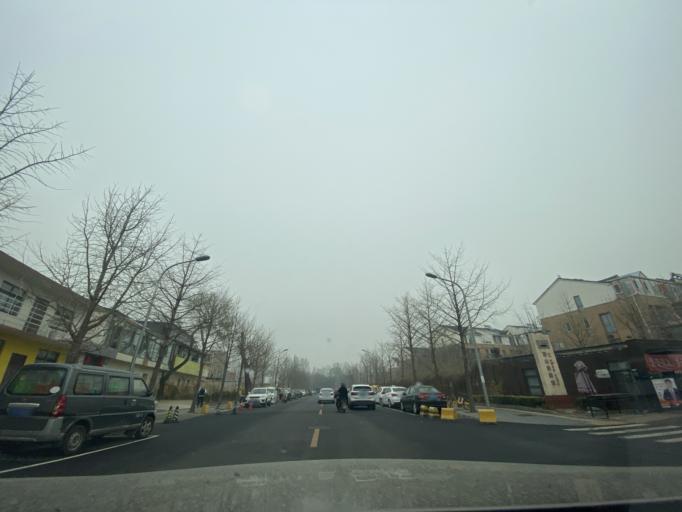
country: CN
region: Beijing
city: Sijiqing
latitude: 39.9565
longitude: 116.2282
